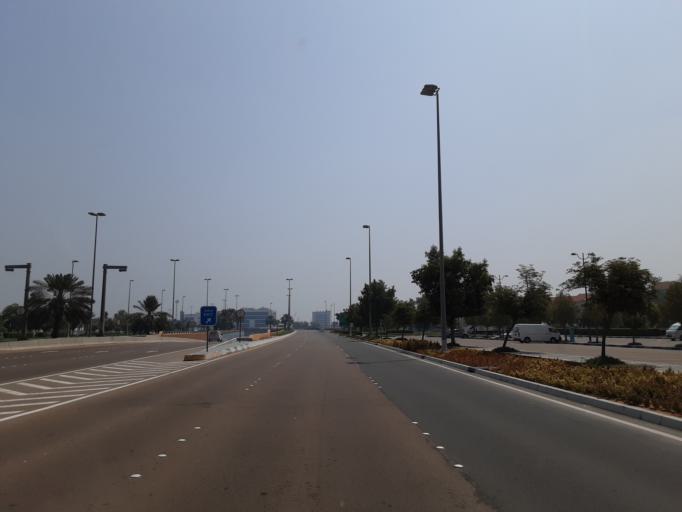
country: AE
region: Abu Dhabi
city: Abu Dhabi
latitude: 24.5102
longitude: 54.3752
